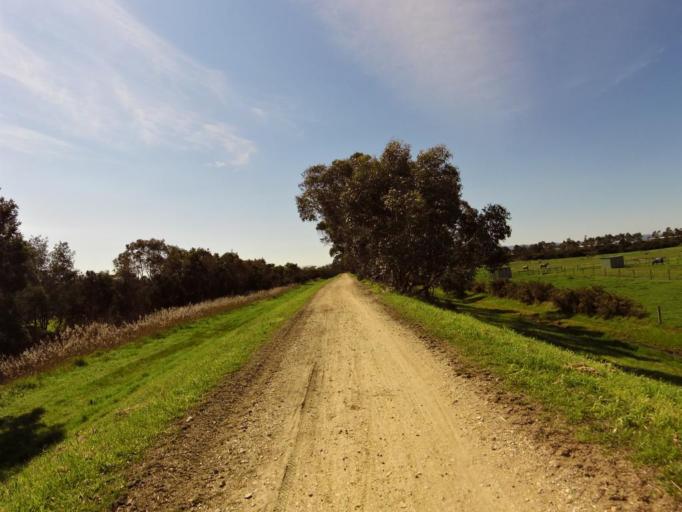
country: AU
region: Victoria
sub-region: Greater Dandenong
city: Keysborough
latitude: -38.0361
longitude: 145.1824
